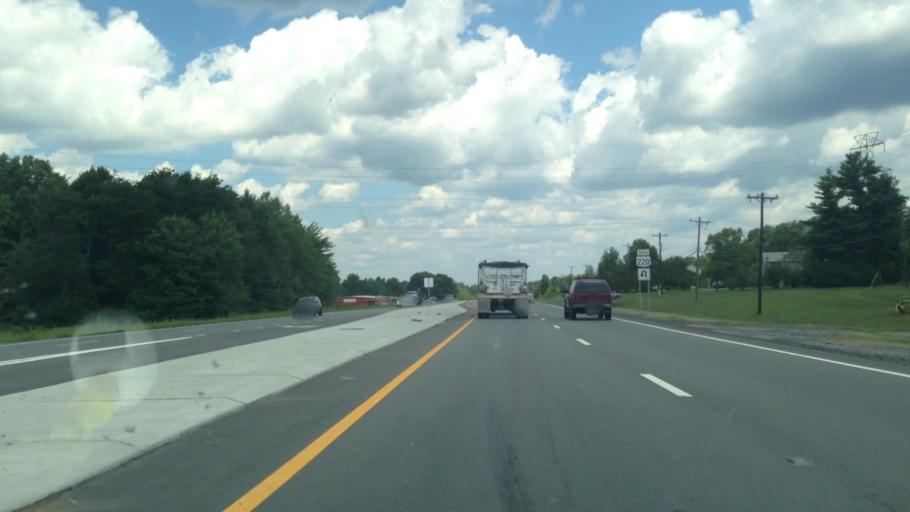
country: US
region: North Carolina
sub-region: Guilford County
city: Stokesdale
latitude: 36.2953
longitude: -79.9394
